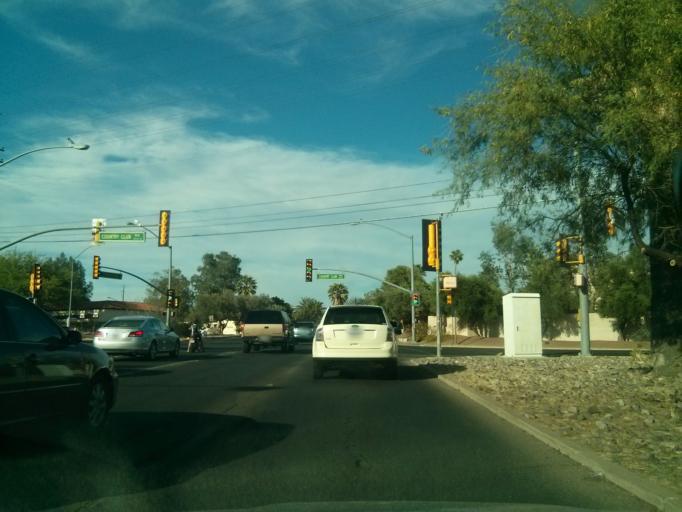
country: US
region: Arizona
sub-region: Pima County
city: Tucson
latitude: 32.2283
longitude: -110.9272
